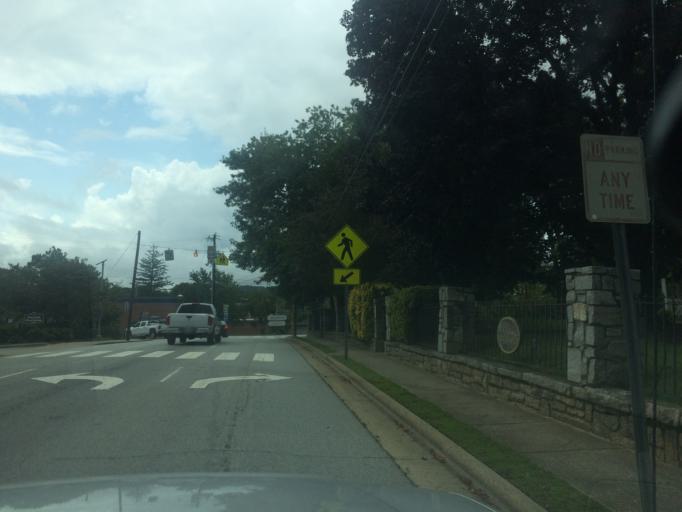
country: US
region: North Carolina
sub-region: Henderson County
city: Hendersonville
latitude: 35.3194
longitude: -82.4629
